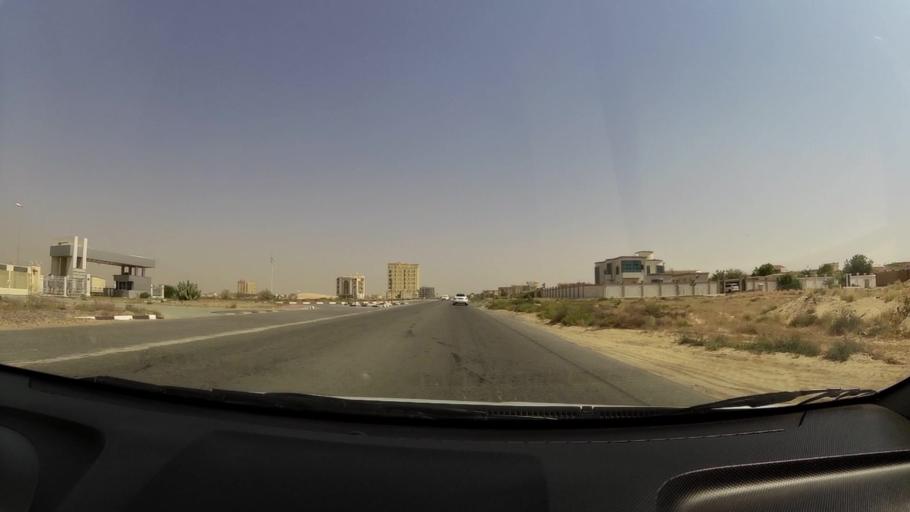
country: AE
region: Umm al Qaywayn
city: Umm al Qaywayn
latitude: 25.4991
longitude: 55.5970
